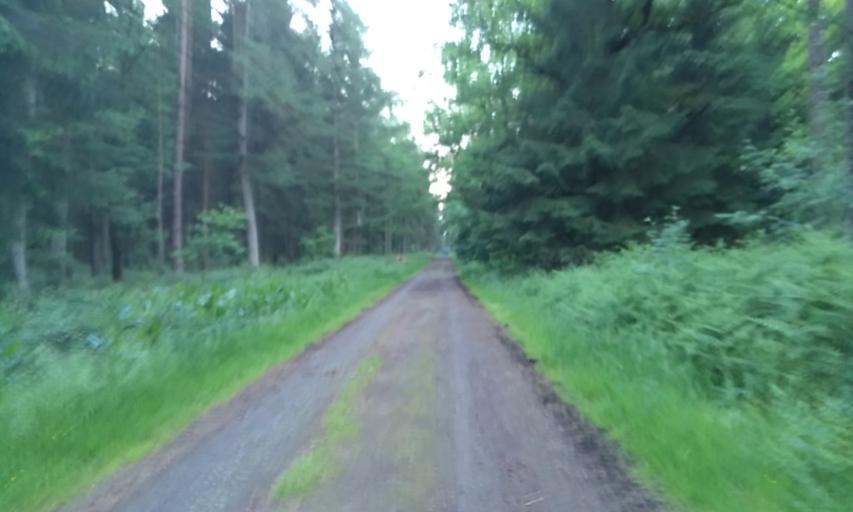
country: DE
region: Lower Saxony
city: Dollern
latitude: 53.5232
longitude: 9.5157
